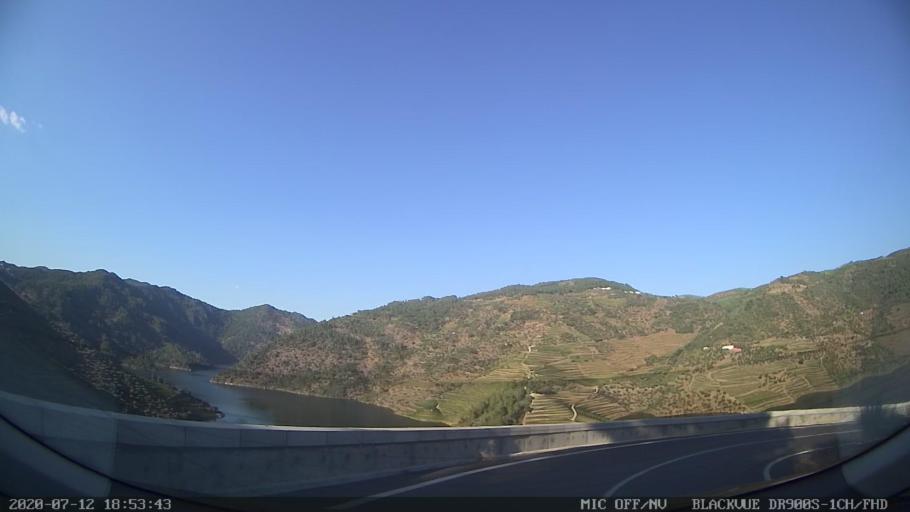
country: PT
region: Viseu
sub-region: Sao Joao da Pesqueira
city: Sao Joao da Pesqueira
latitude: 41.2312
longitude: -7.4269
